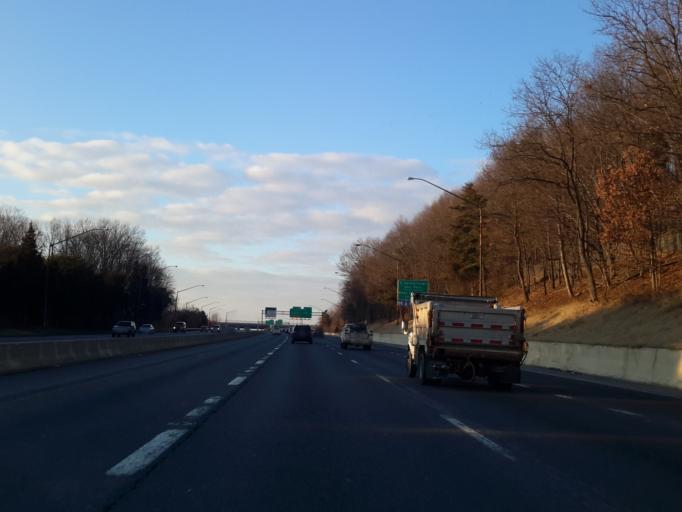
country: US
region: Maryland
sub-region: Montgomery County
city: Germantown
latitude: 39.1785
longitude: -77.2493
